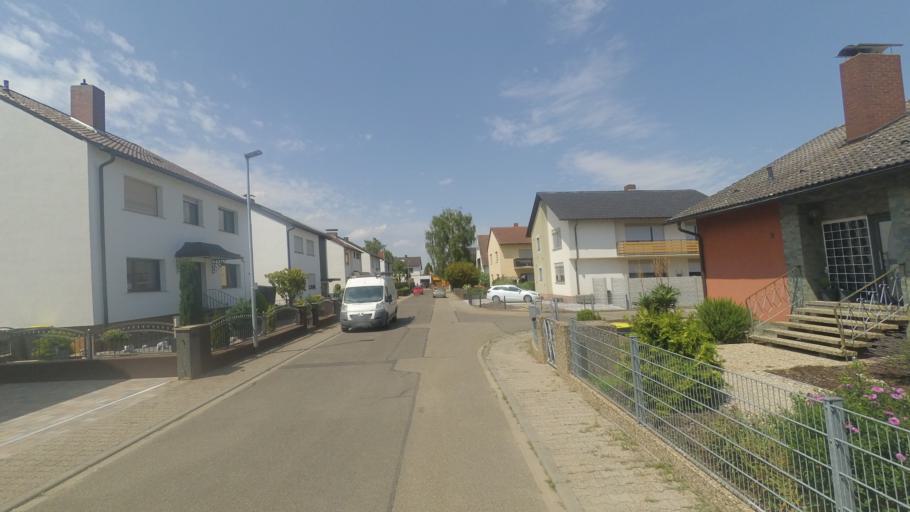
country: DE
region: Rheinland-Pfalz
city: Frankenthal
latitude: 49.5104
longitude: 8.3378
